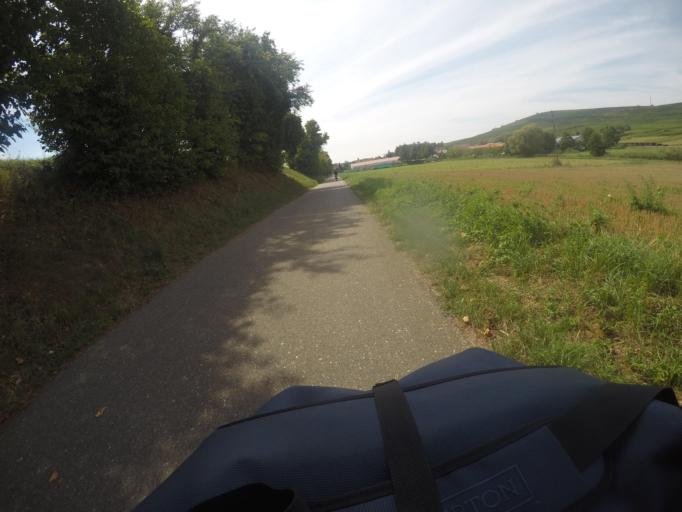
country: DE
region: Baden-Wuerttemberg
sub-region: Freiburg Region
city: Schallstadt
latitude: 47.9451
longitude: 7.7579
